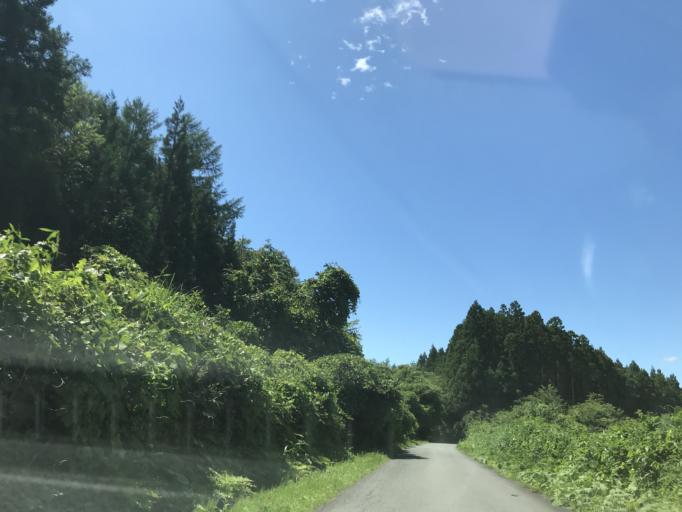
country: JP
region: Iwate
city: Ichinoseki
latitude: 38.9337
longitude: 141.0289
